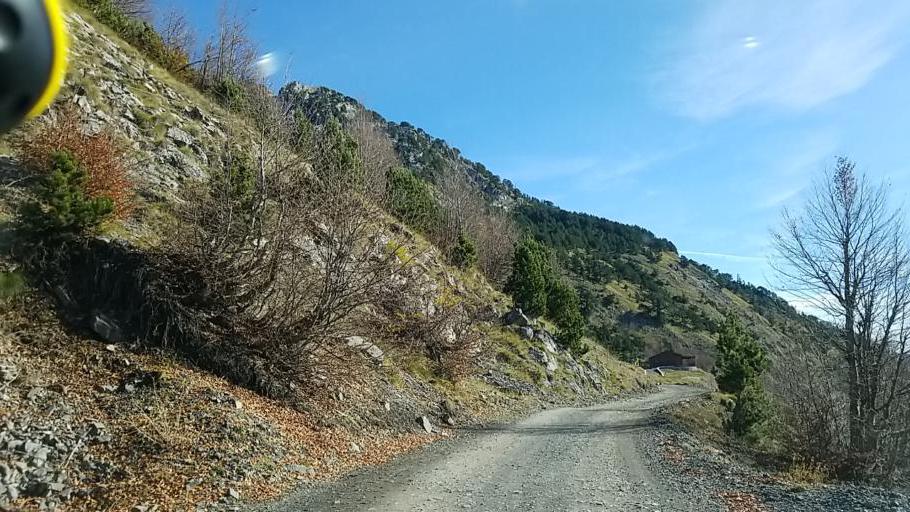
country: AL
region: Shkoder
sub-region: Rrethi i Shkodres
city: Nicaj-Shale
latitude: 42.3893
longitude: 19.7231
